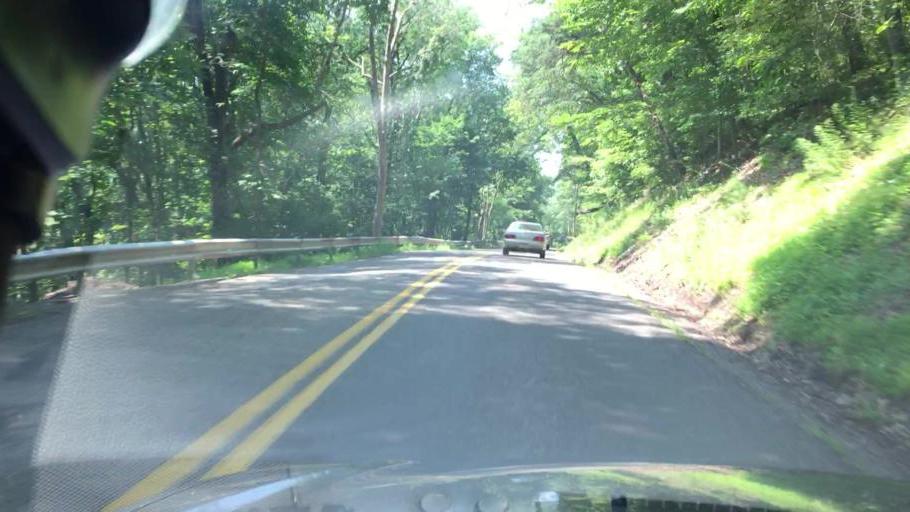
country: US
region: Pennsylvania
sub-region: Columbia County
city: Espy
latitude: 40.9758
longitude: -76.3997
